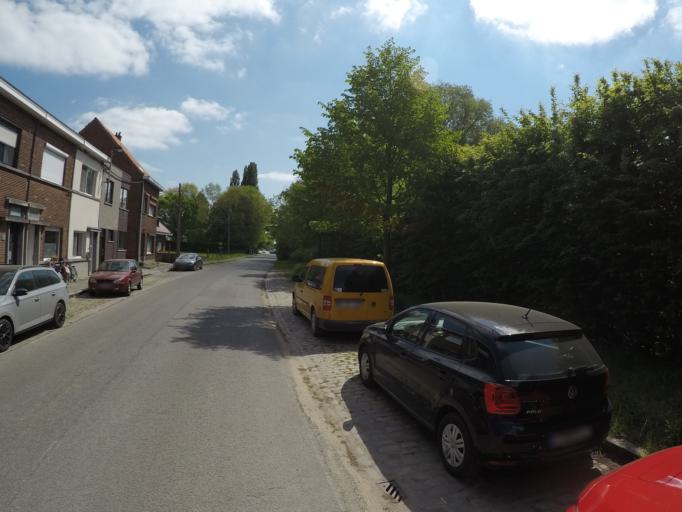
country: BE
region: Flanders
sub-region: Provincie Antwerpen
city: Lier
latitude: 51.1281
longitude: 4.5940
